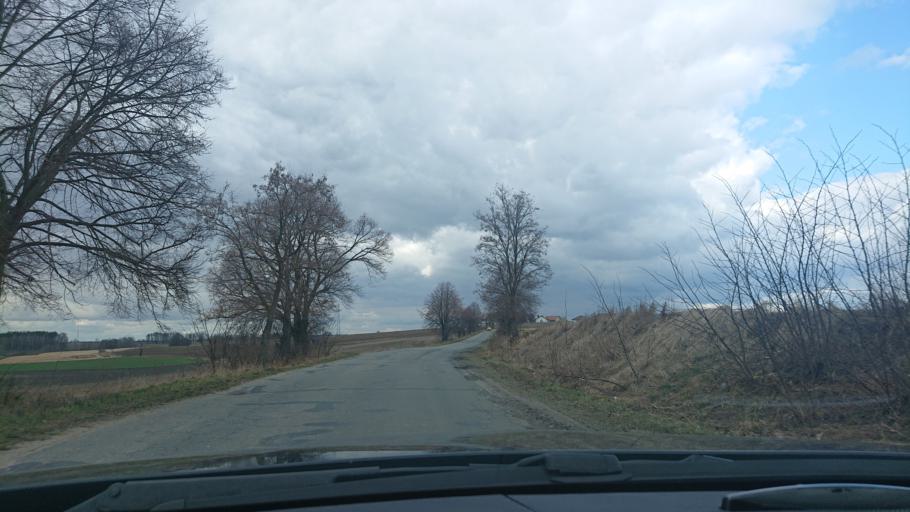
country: PL
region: Greater Poland Voivodeship
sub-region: Powiat gnieznienski
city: Niechanowo
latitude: 52.5564
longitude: 17.6968
